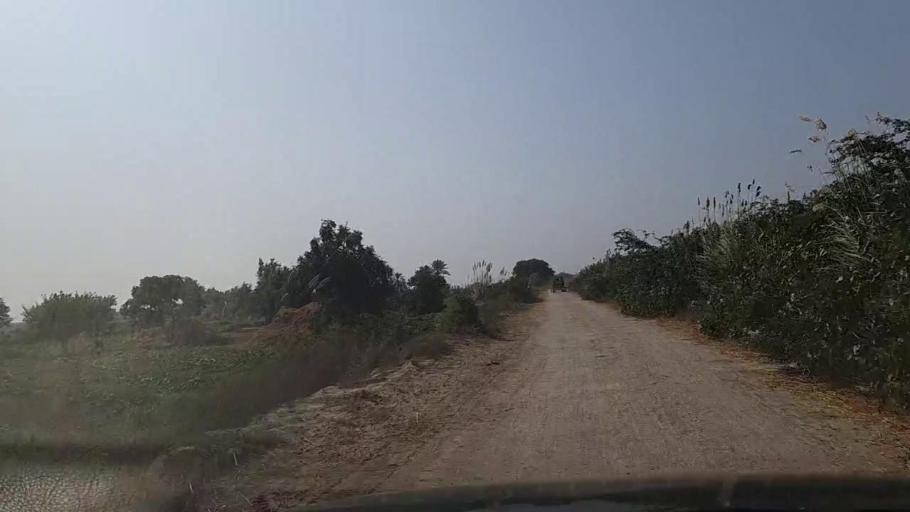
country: PK
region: Sindh
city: Gharo
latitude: 24.7065
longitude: 67.6482
